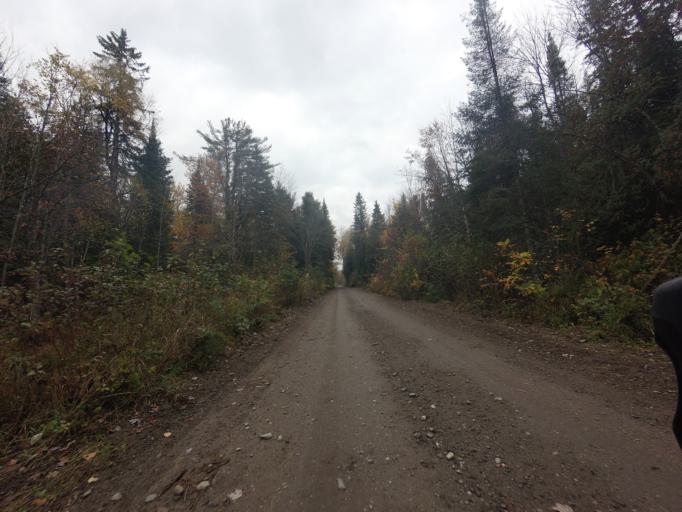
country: CA
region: Ontario
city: Renfrew
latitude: 45.1756
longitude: -76.6821
